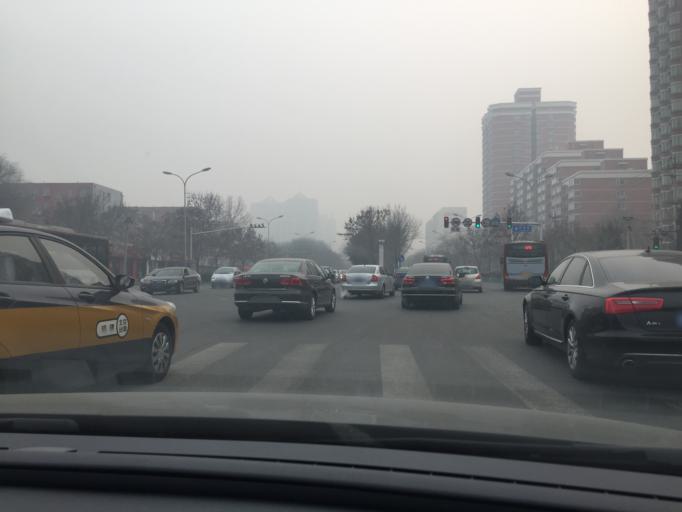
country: CN
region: Beijing
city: Qinghe
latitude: 40.0066
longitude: 116.3462
